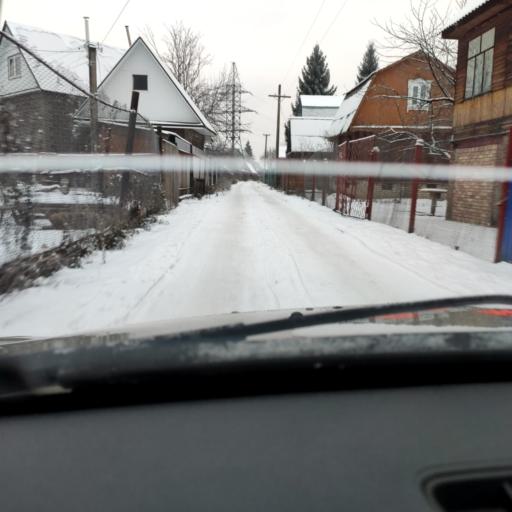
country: RU
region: Bashkortostan
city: Ufa
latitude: 54.6937
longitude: 55.8946
